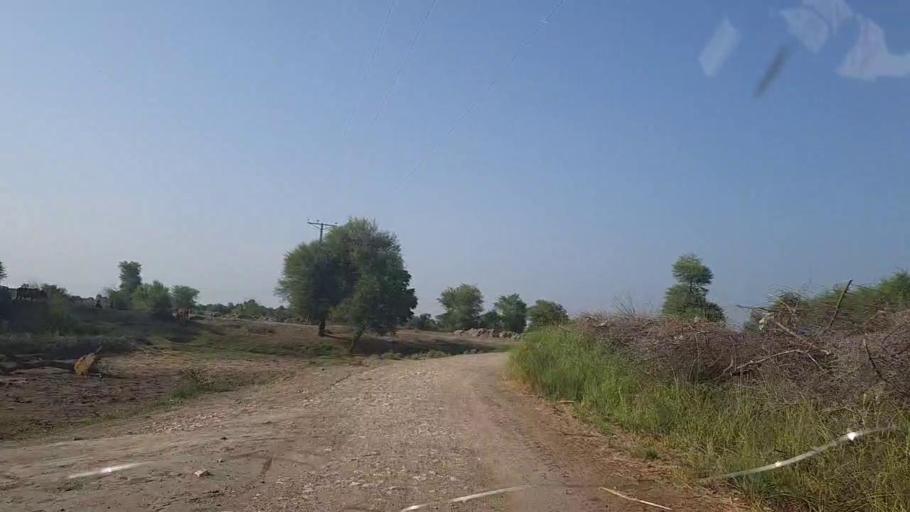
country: PK
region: Sindh
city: Khanpur
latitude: 27.7077
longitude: 69.3317
